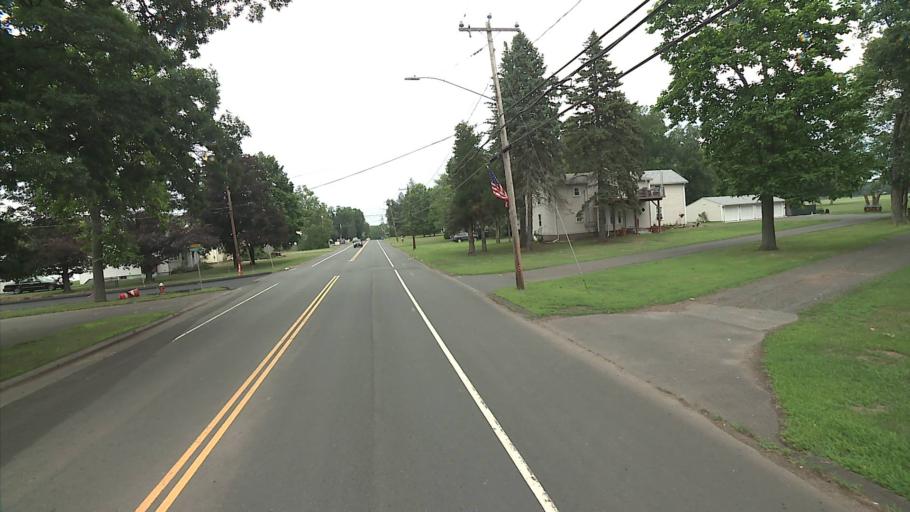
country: US
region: Connecticut
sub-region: Middlesex County
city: Cromwell
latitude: 41.6306
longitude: -72.6505
